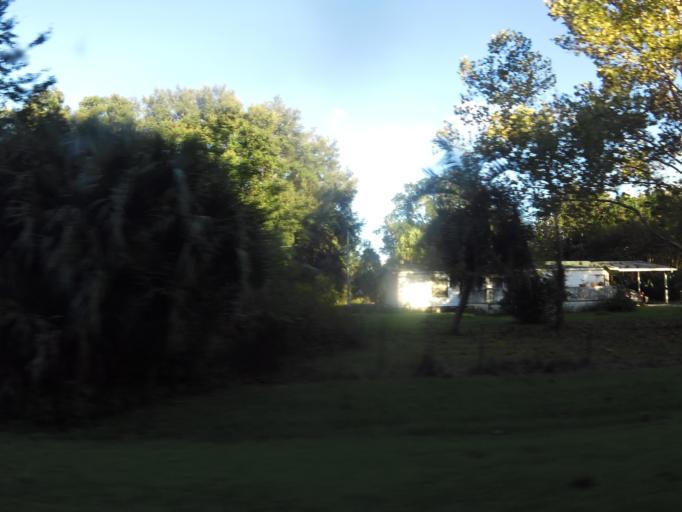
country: US
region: Florida
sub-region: Marion County
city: Citra
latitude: 29.4553
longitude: -82.1056
